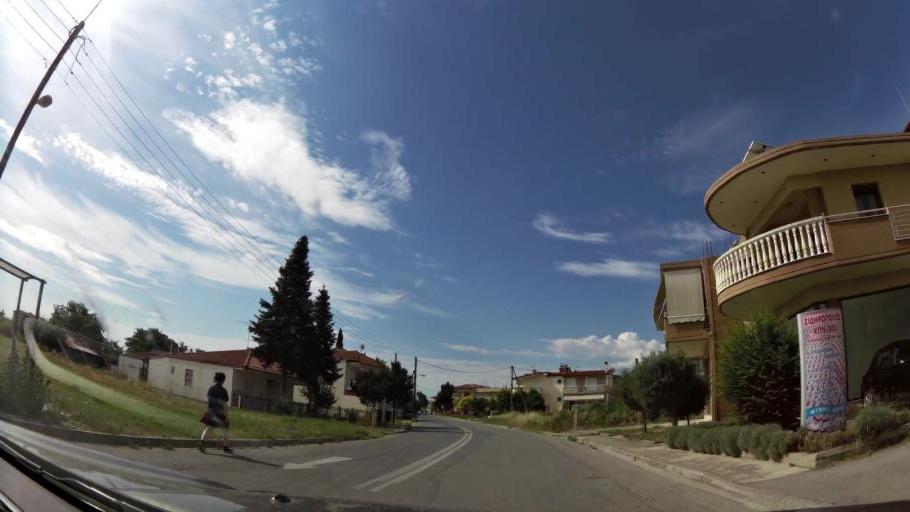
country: GR
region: Central Macedonia
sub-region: Nomos Pierias
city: Katerini
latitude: 40.2851
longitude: 22.5033
